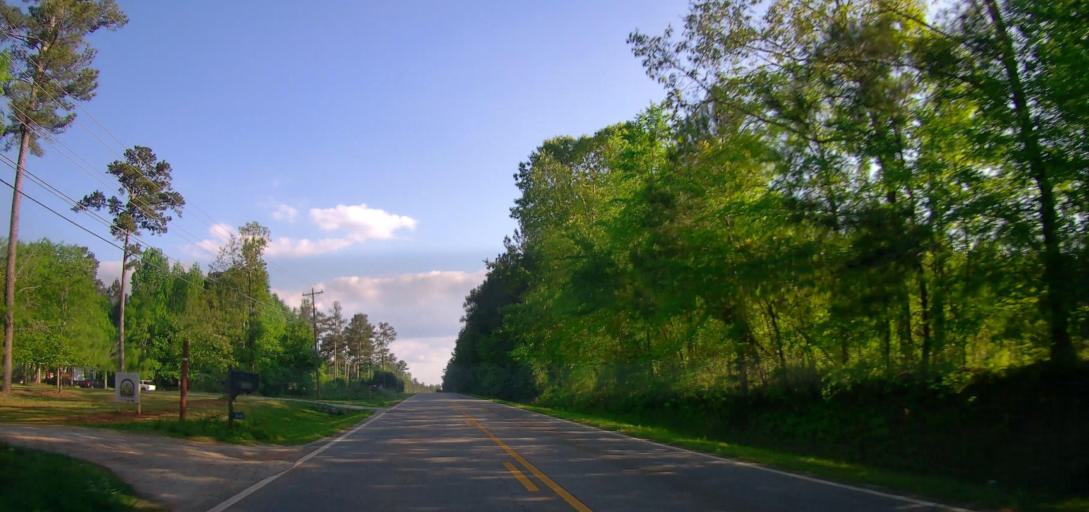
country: US
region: Georgia
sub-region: Putnam County
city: Eatonton
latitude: 33.2643
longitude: -83.3013
